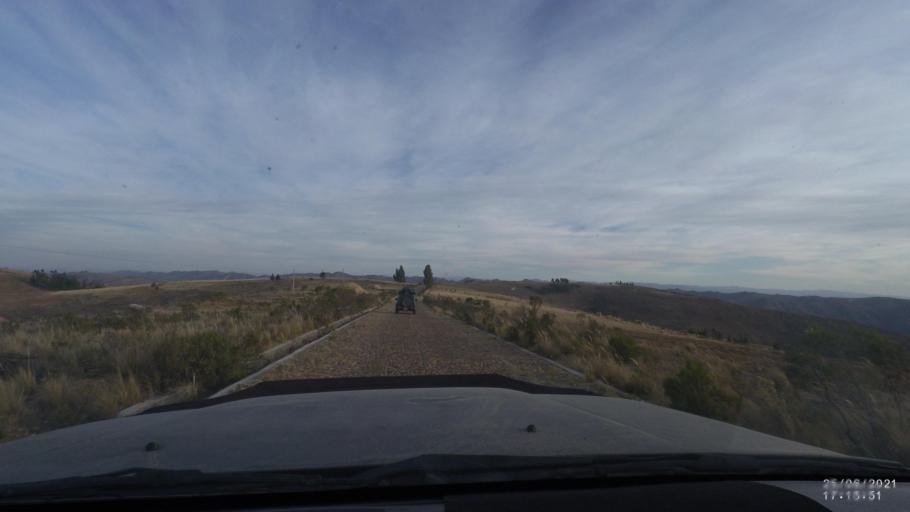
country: BO
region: Cochabamba
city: Arani
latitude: -17.8768
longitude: -65.6987
